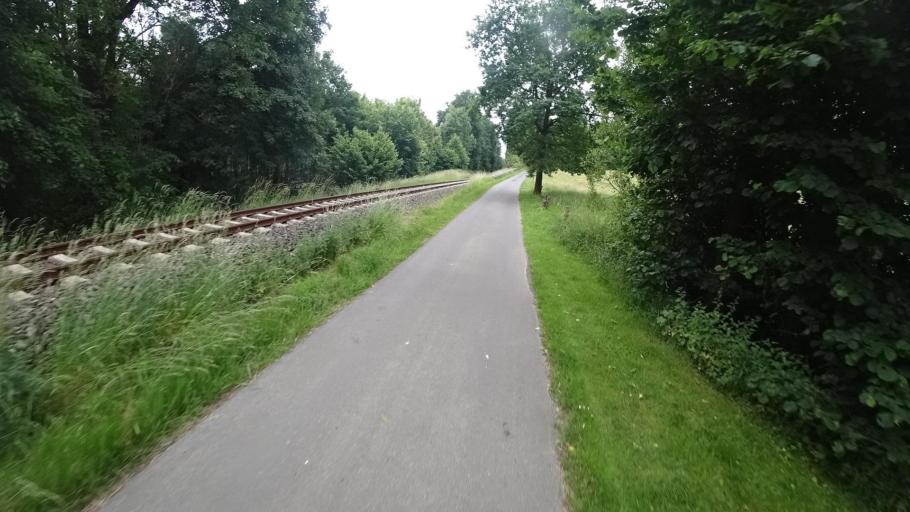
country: DE
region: Rheinland-Pfalz
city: Bachenberg
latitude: 50.7107
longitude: 7.6579
